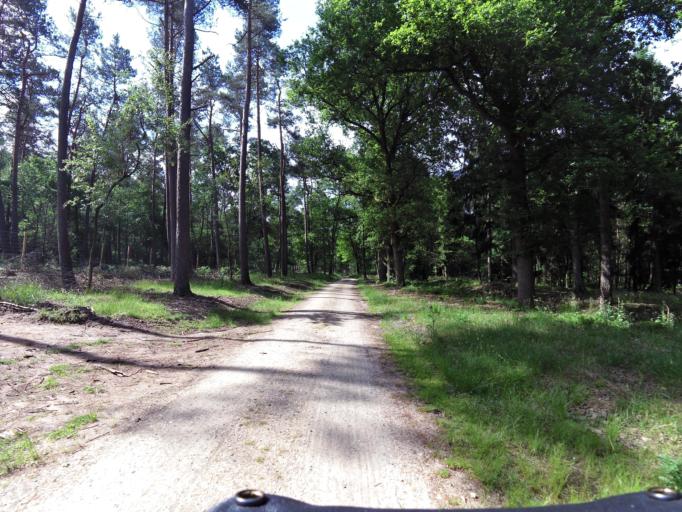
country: NL
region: Gelderland
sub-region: Gemeente Apeldoorn
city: Loenen
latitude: 52.1202
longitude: 5.9963
